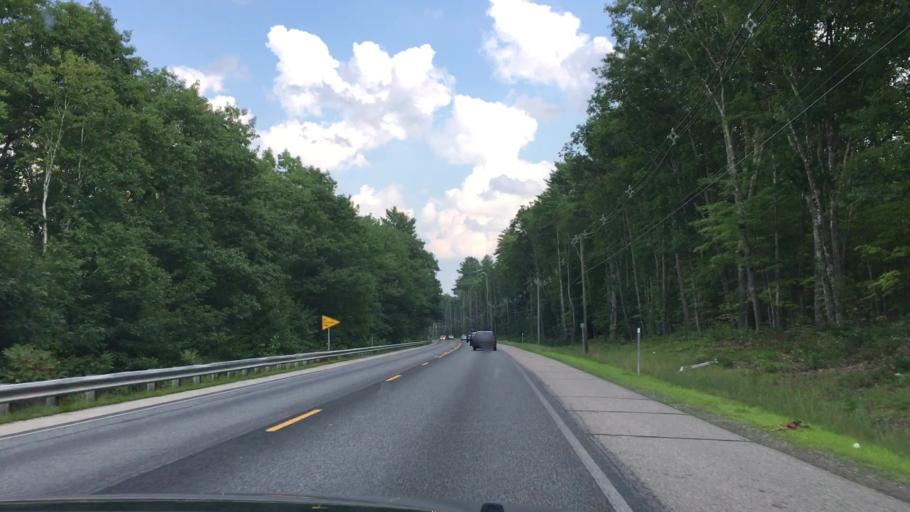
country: US
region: New Hampshire
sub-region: Strafford County
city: Farmington
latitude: 43.3809
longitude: -71.0692
